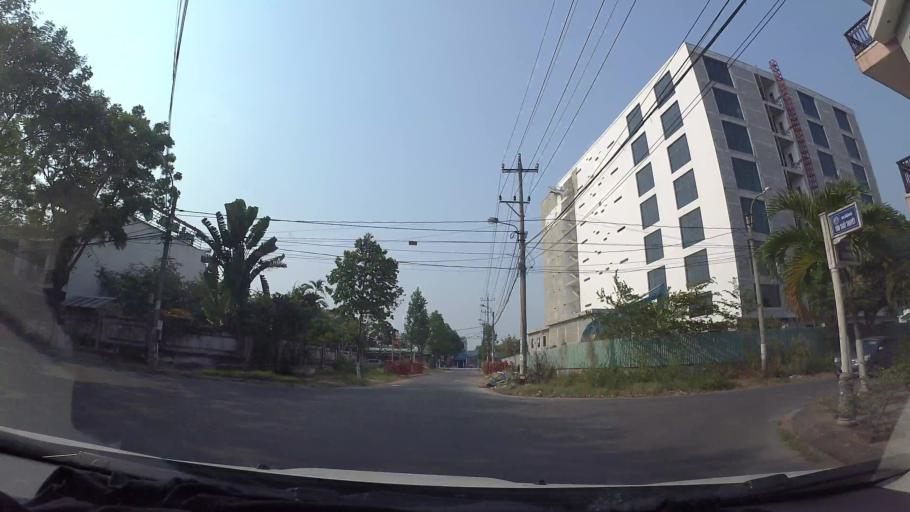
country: VN
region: Da Nang
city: Cam Le
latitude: 16.0230
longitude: 108.2084
